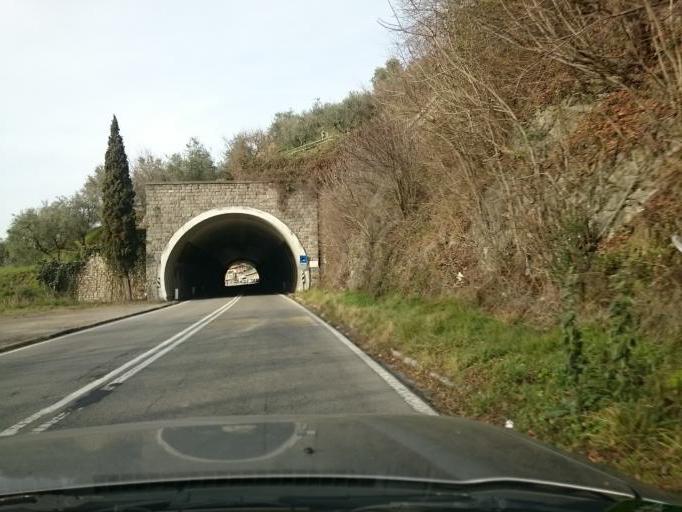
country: IT
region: Lombardy
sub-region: Provincia di Brescia
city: Marone
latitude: 45.7526
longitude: 10.0842
